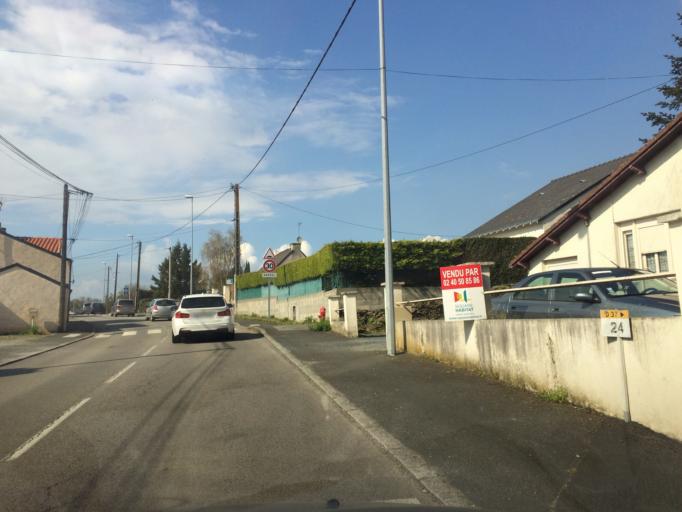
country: FR
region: Pays de la Loire
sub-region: Departement de la Loire-Atlantique
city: Carquefou
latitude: 47.3104
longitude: -1.5076
